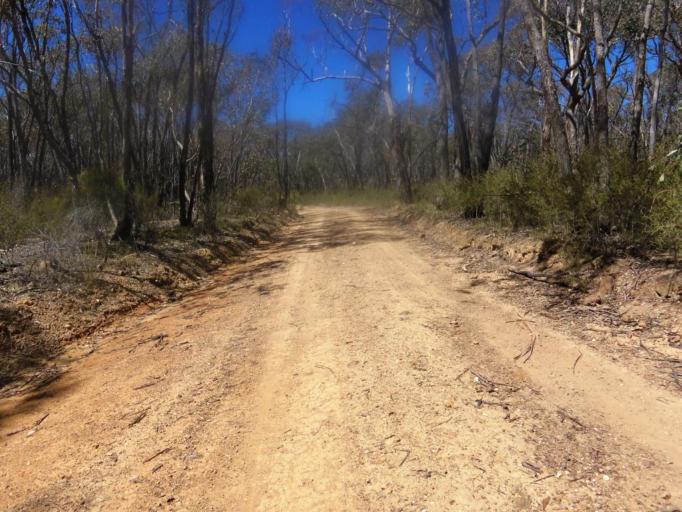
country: AU
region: Victoria
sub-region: Mount Alexander
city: Castlemaine
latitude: -36.9970
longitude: 144.1043
